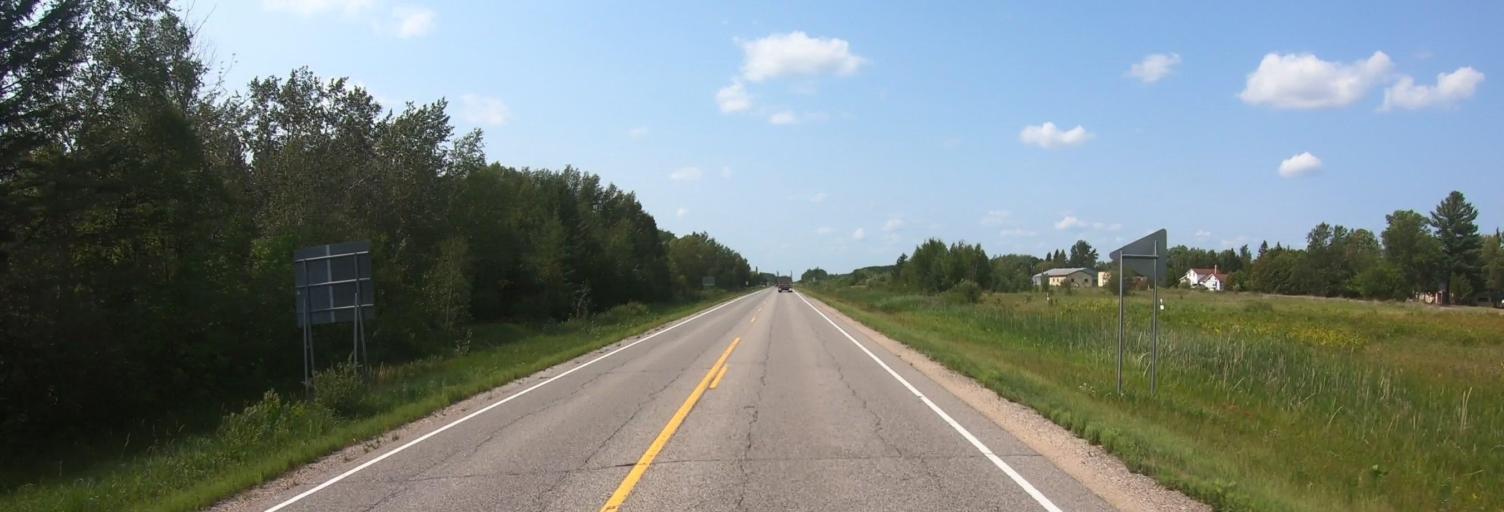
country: US
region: Minnesota
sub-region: Roseau County
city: Warroad
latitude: 48.8000
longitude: -95.0926
